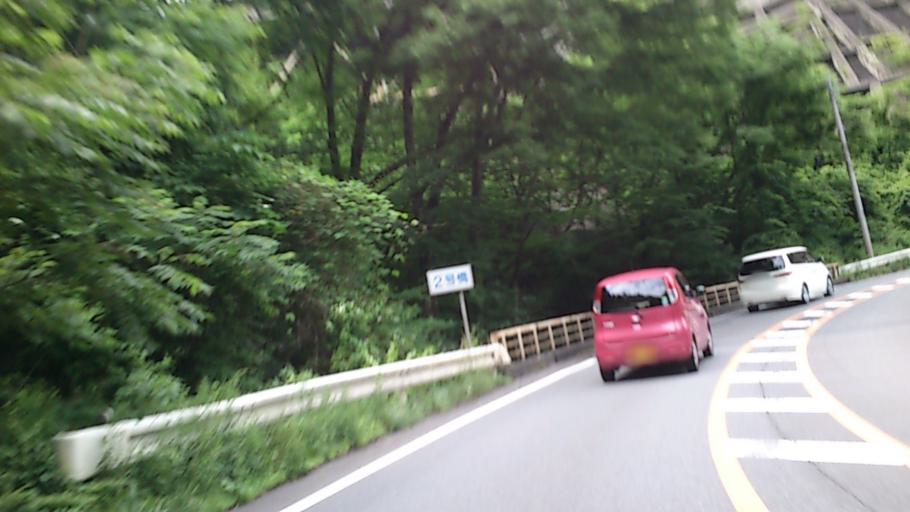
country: JP
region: Nagano
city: Saku
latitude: 36.2266
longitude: 138.6311
